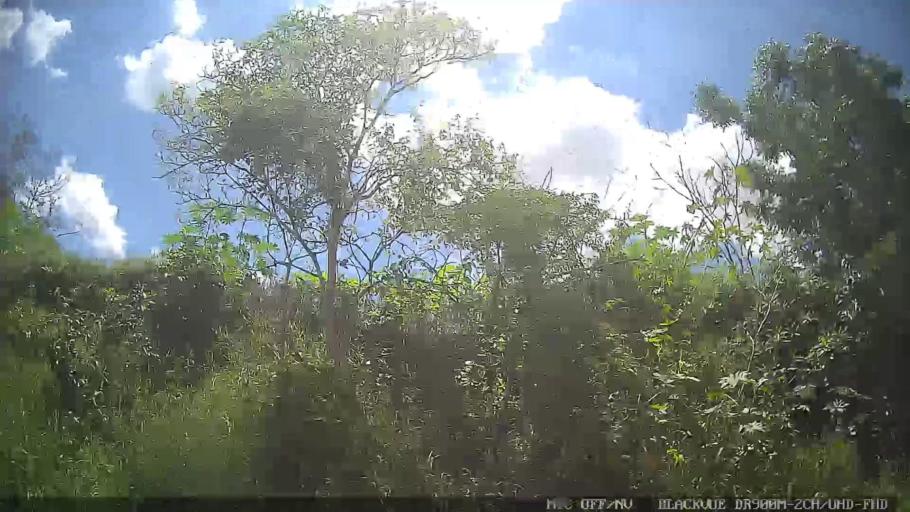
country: BR
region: Sao Paulo
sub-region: Itatiba
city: Itatiba
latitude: -22.8596
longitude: -46.7855
